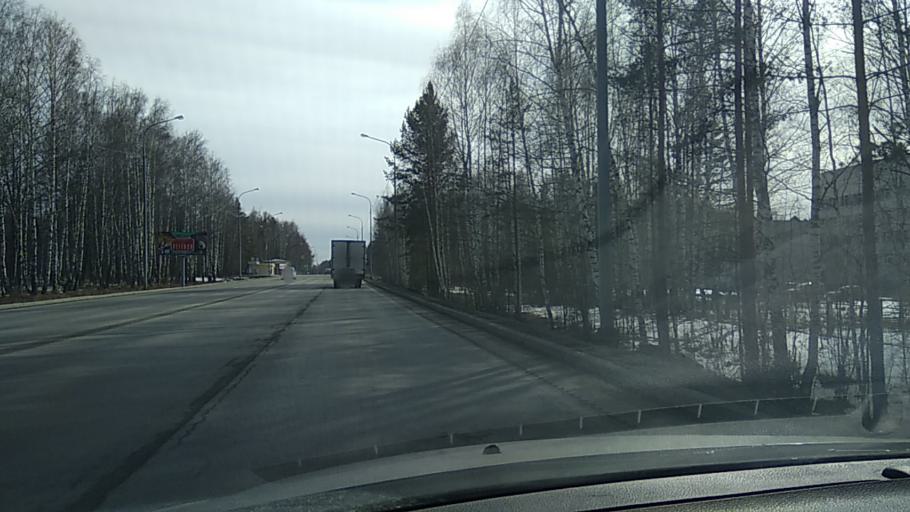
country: RU
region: Sverdlovsk
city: Nikolo-Pavlovskoye
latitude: 57.8553
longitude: 60.0313
